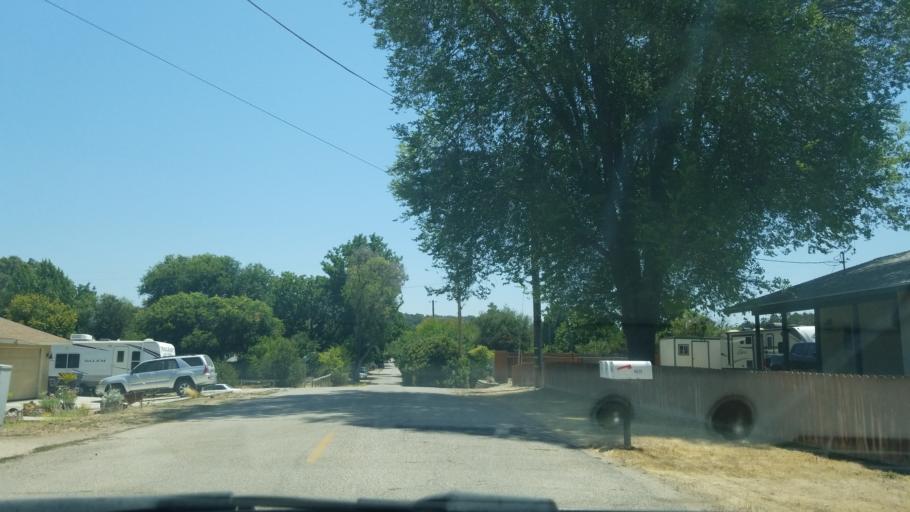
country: US
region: California
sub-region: San Luis Obispo County
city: Atascadero
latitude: 35.5070
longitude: -120.6668
